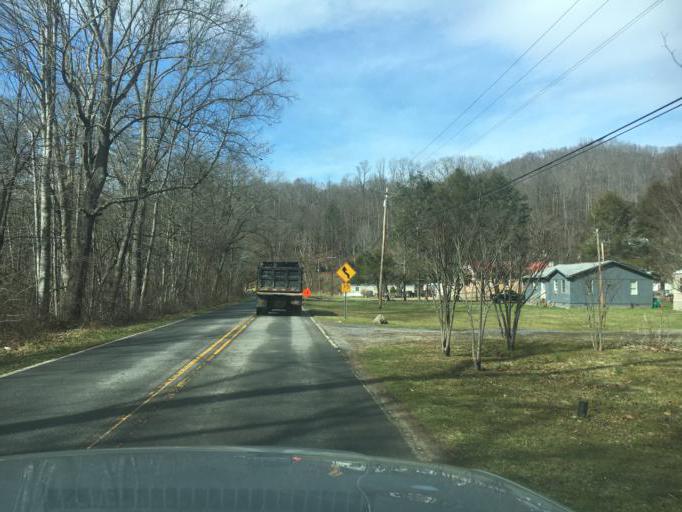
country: US
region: North Carolina
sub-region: Haywood County
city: Canton
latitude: 35.4512
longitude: -82.8225
